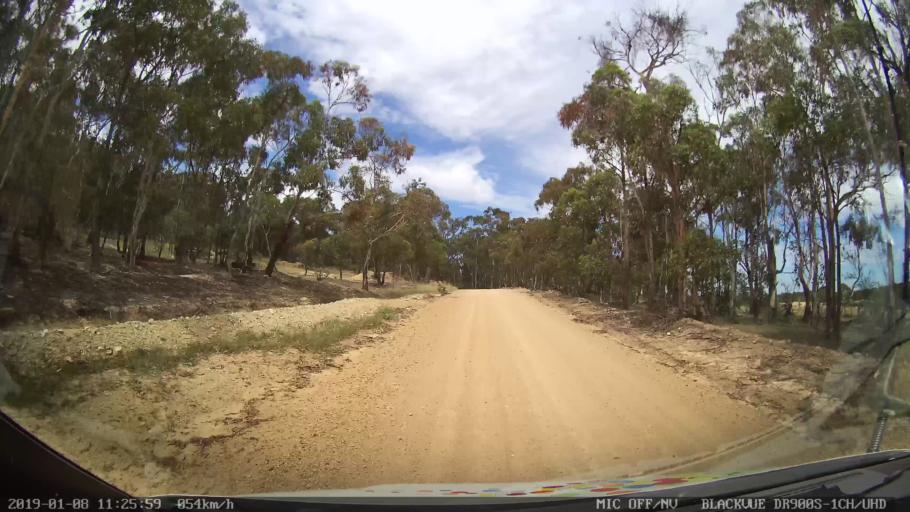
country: AU
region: New South Wales
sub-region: Guyra
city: Guyra
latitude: -30.2771
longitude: 151.5593
